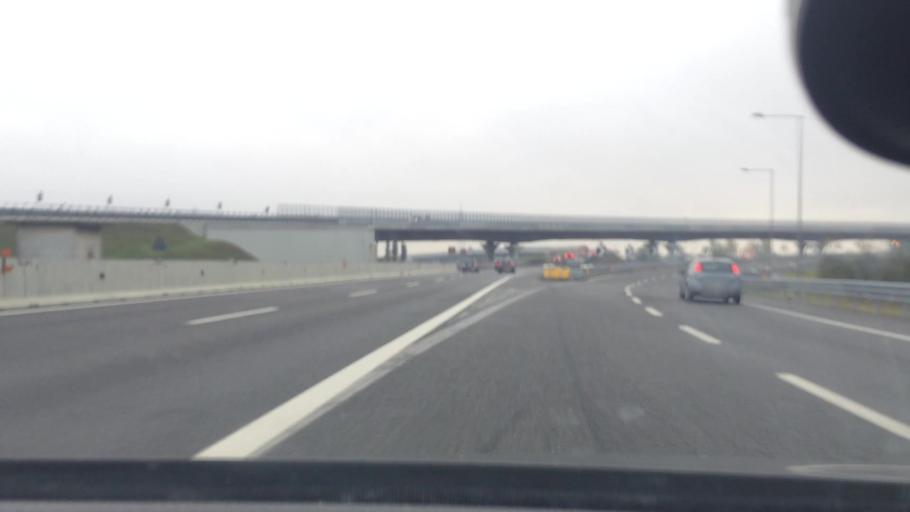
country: IT
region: Lombardy
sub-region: Provincia di Varese
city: Origgio
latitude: 45.5804
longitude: 9.0106
